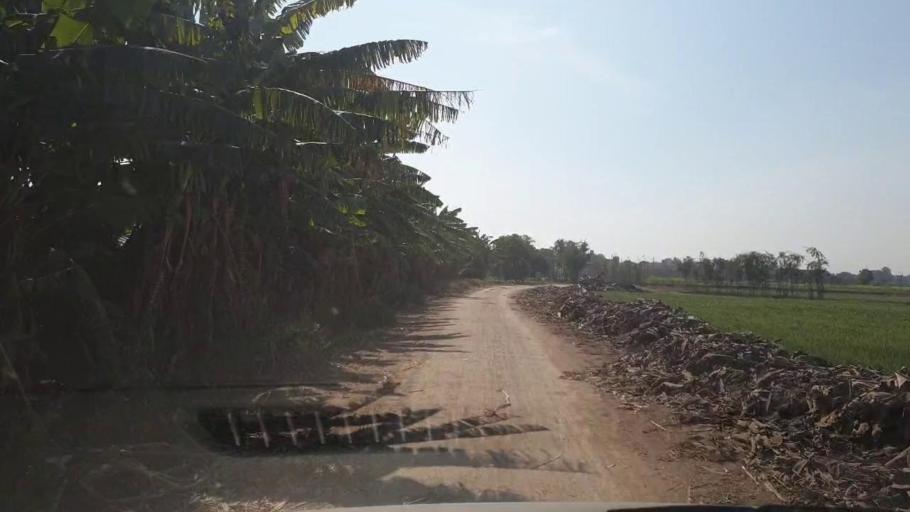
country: PK
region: Sindh
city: Tando Allahyar
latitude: 25.3927
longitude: 68.7818
